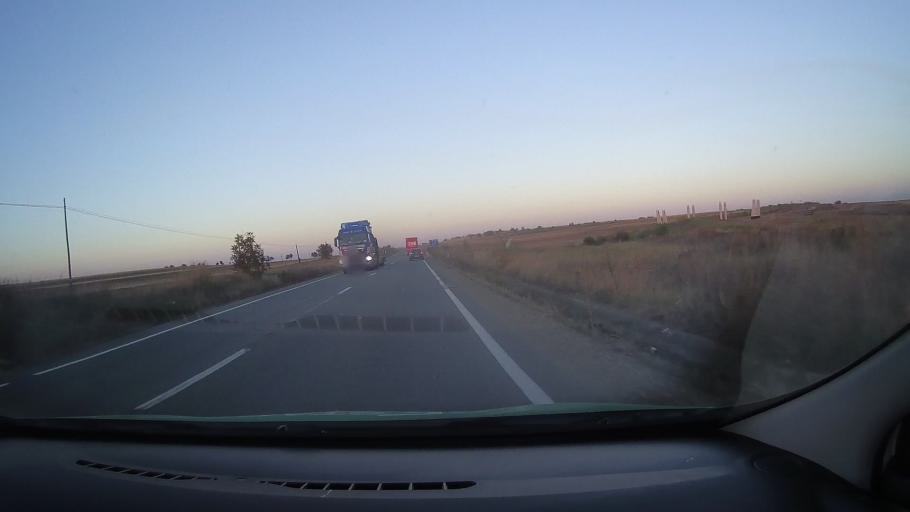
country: RO
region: Bihor
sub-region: Comuna Cherechiu
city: Cherechiu
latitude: 47.3723
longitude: 22.1324
